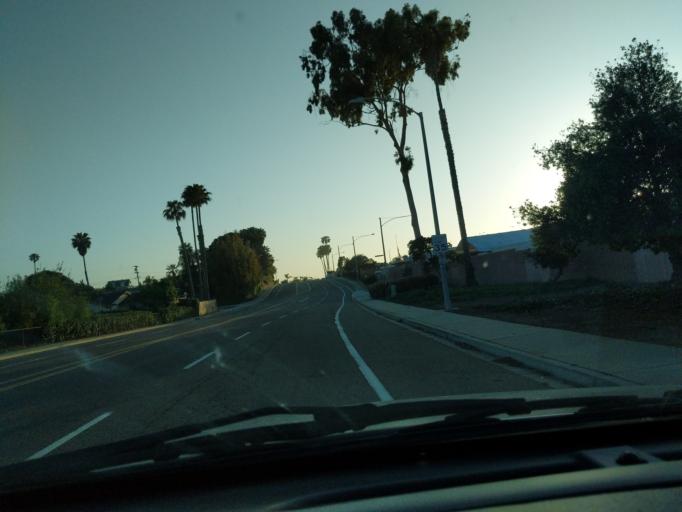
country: US
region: California
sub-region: San Diego County
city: Carlsbad
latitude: 33.1336
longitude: -117.3324
